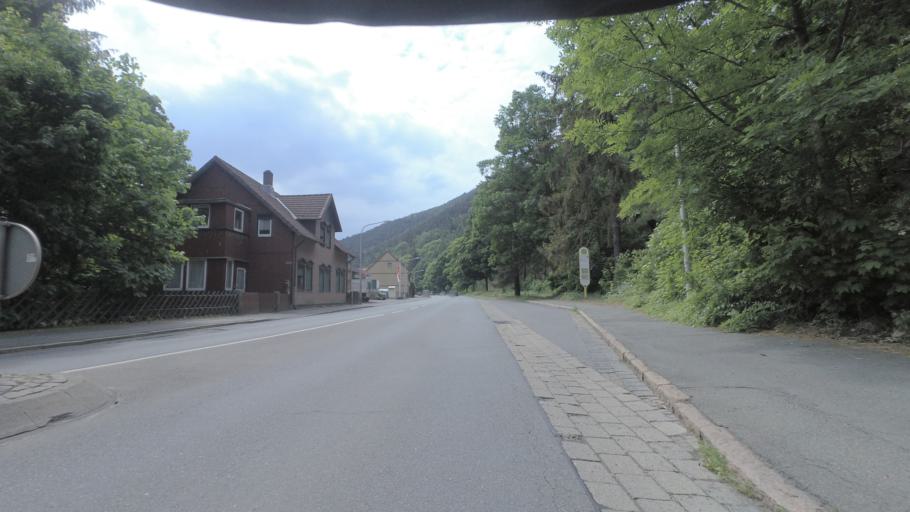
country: DE
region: Lower Saxony
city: Goslar
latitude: 51.8936
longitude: 10.4789
